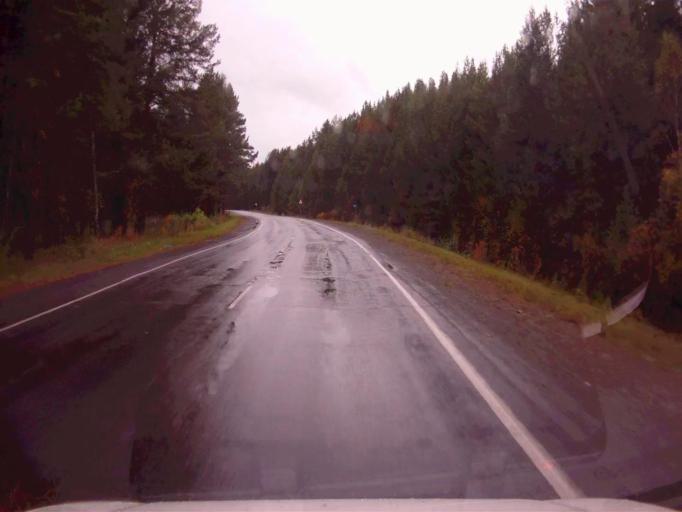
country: RU
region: Chelyabinsk
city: Verkhniy Ufaley
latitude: 56.0238
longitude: 60.2985
